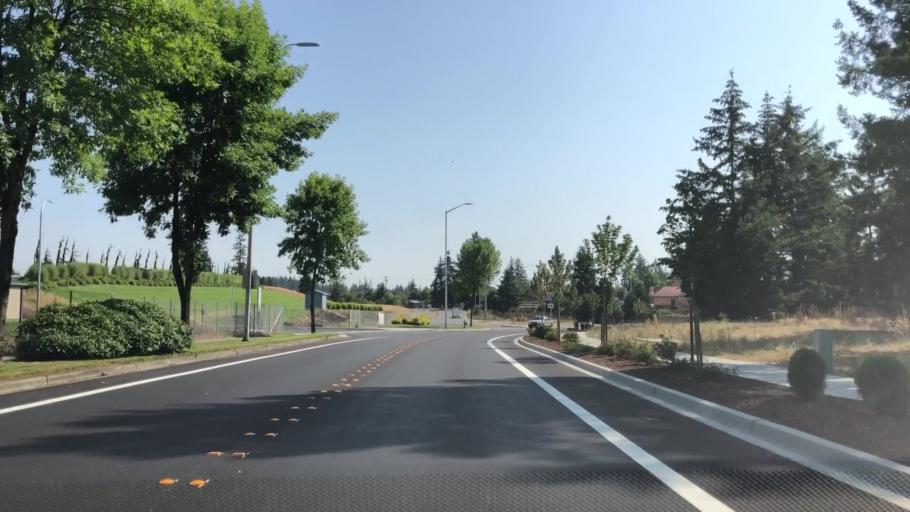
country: US
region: Washington
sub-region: Thurston County
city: Tanglewilde-Thompson Place
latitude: 47.0676
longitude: -122.7646
